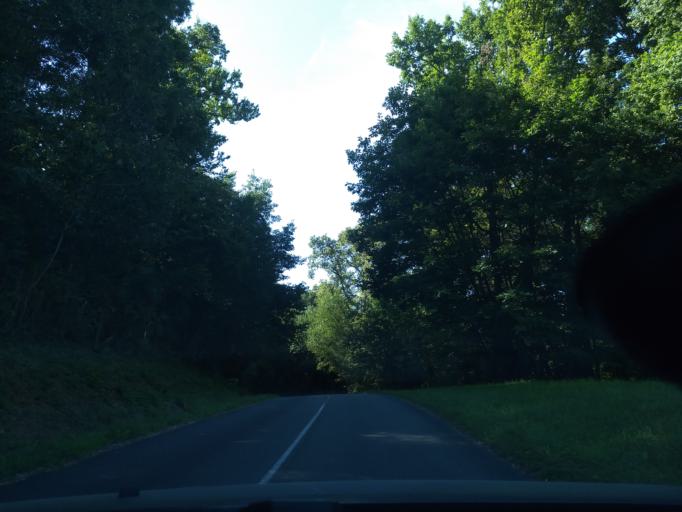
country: FR
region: Aquitaine
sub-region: Departement des Pyrenees-Atlantiques
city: Soumoulou
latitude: 43.2912
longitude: -0.1487
